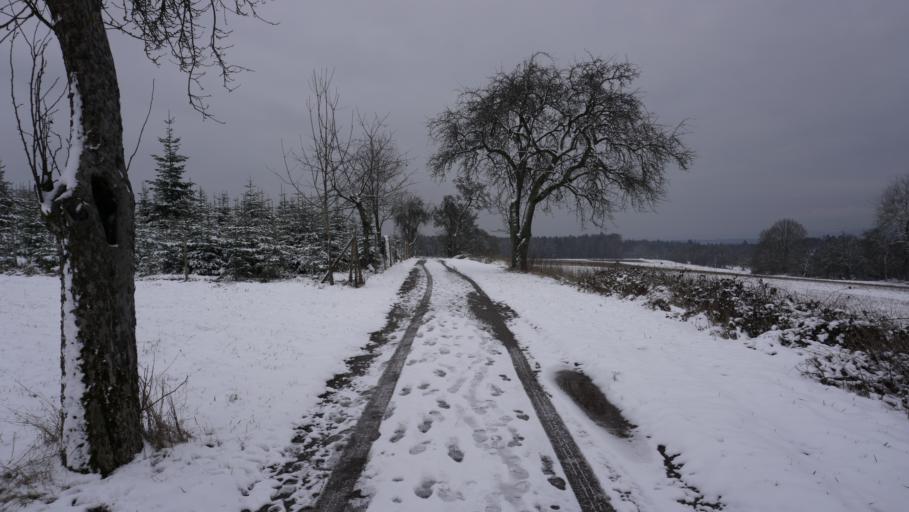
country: DE
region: Baden-Wuerttemberg
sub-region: Karlsruhe Region
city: Neckargerach
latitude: 49.4416
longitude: 9.0965
